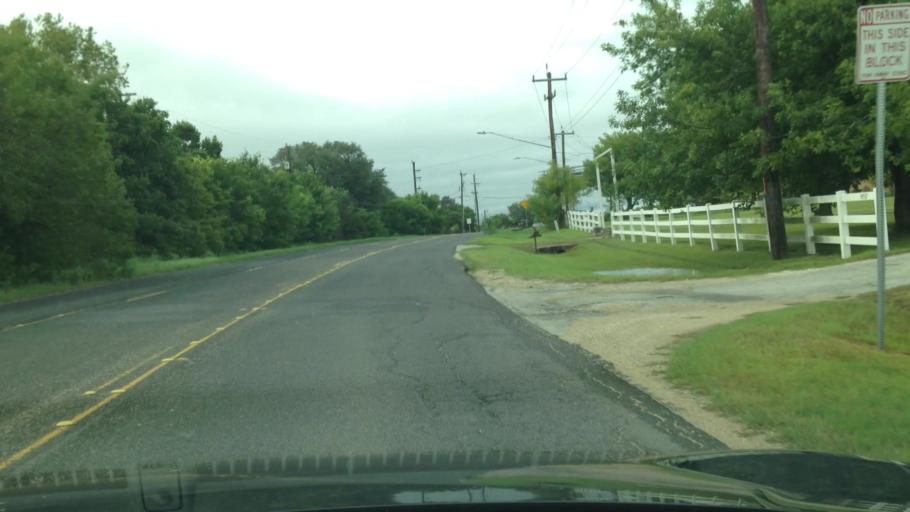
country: US
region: Texas
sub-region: Bexar County
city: Windcrest
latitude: 29.5740
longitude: -98.4182
